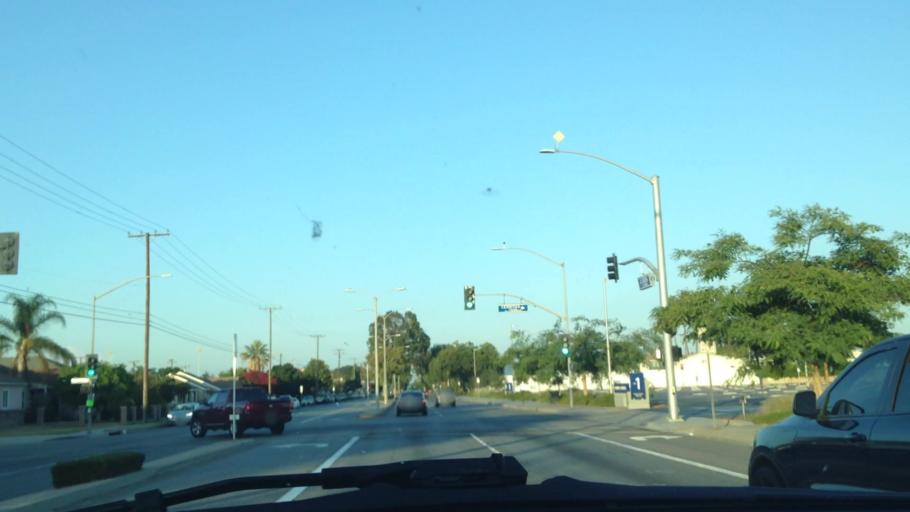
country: US
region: California
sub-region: Los Angeles County
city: Norwalk
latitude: 33.8875
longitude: -118.0917
